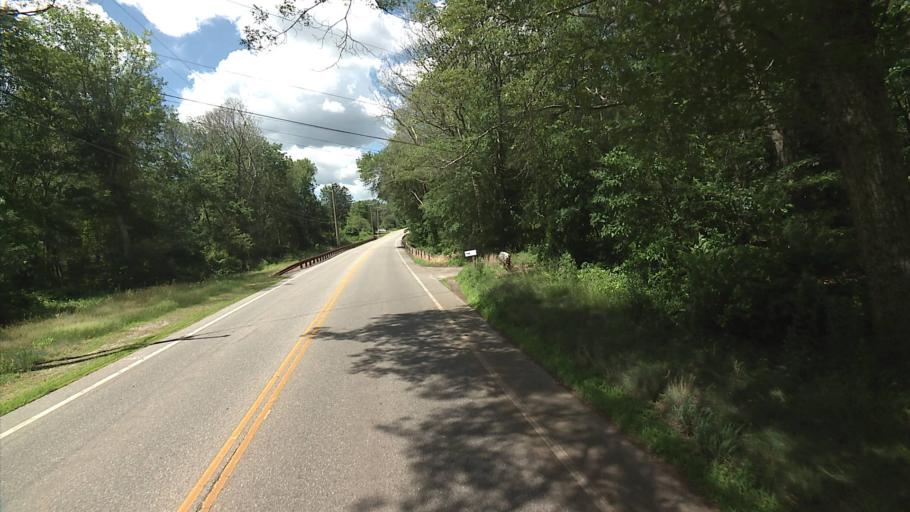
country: US
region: Rhode Island
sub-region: Washington County
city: Ashaway
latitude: 41.4375
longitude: -71.8093
